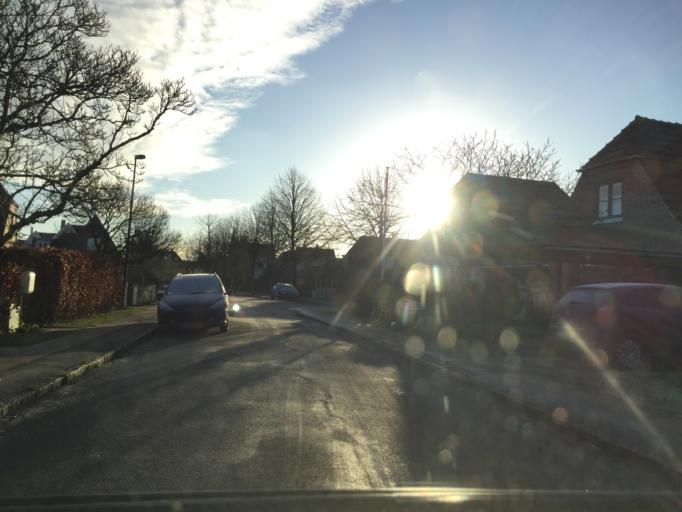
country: DK
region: Capital Region
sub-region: Kobenhavn
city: Vanlose
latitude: 55.6624
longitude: 12.5012
